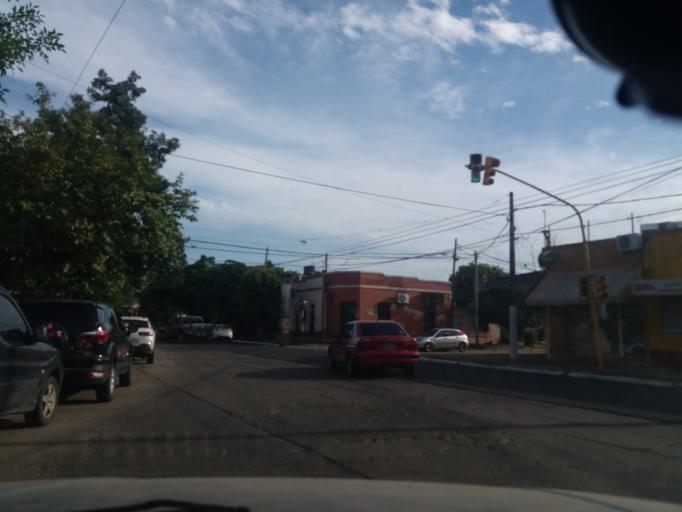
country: AR
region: Corrientes
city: Corrientes
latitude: -27.4844
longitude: -58.8323
